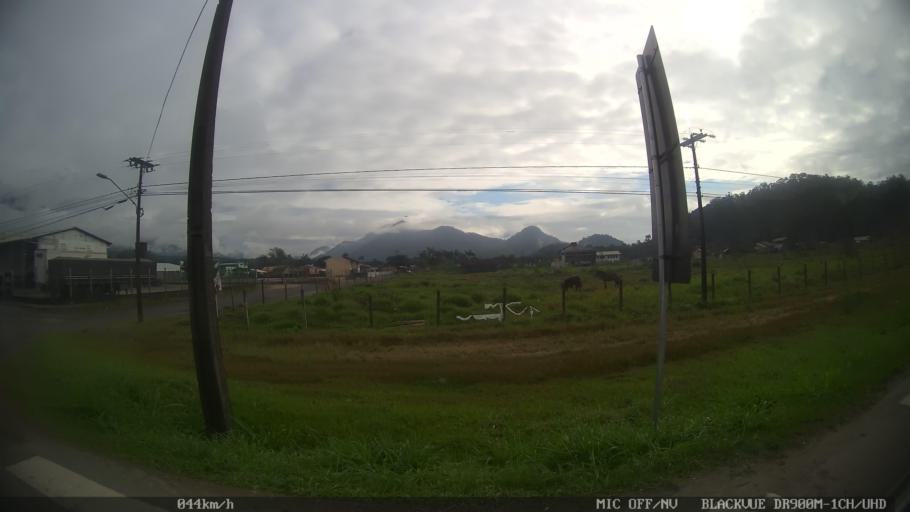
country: BR
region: Santa Catarina
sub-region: Joinville
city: Joinville
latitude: -26.0293
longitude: -48.8500
